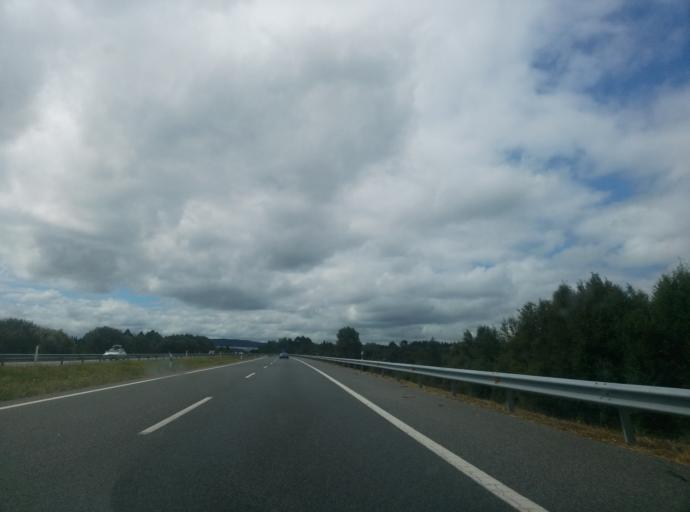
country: ES
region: Galicia
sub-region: Provincia de Lugo
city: Begonte
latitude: 43.1688
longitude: -7.6975
